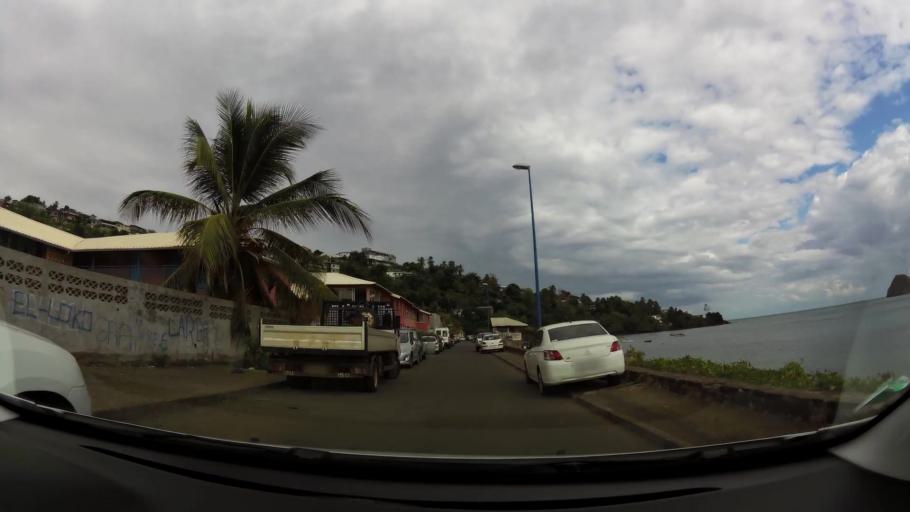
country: YT
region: Sada
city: Sada
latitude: -12.8502
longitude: 45.0980
